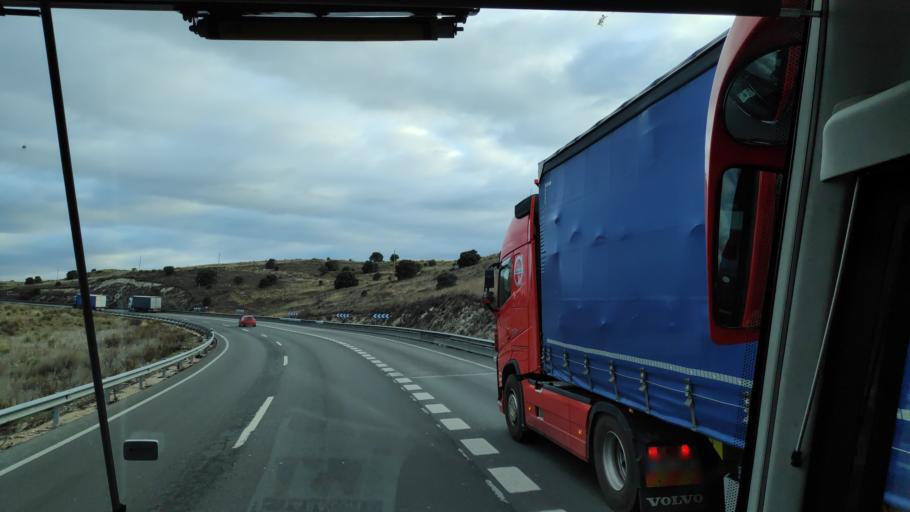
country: ES
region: Madrid
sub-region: Provincia de Madrid
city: Tielmes
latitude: 40.2006
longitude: -3.3148
